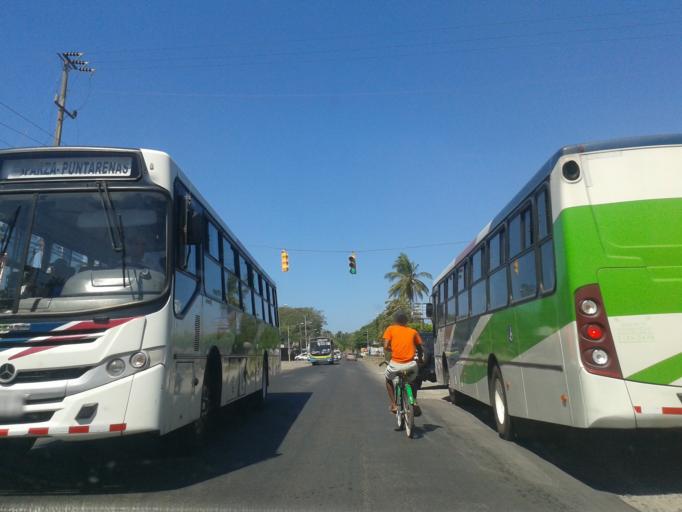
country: CR
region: Puntarenas
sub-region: Canton Central de Puntarenas
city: Chacarita
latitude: 9.9780
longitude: -84.7350
